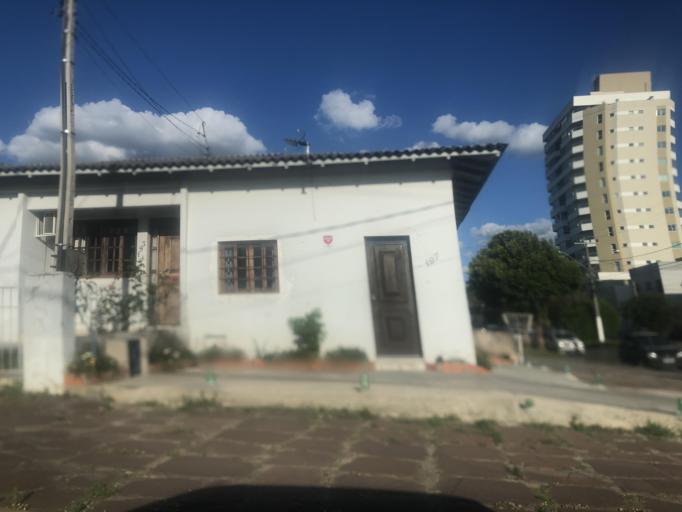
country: BR
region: Santa Catarina
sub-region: Lages
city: Lages
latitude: -27.8135
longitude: -50.3136
